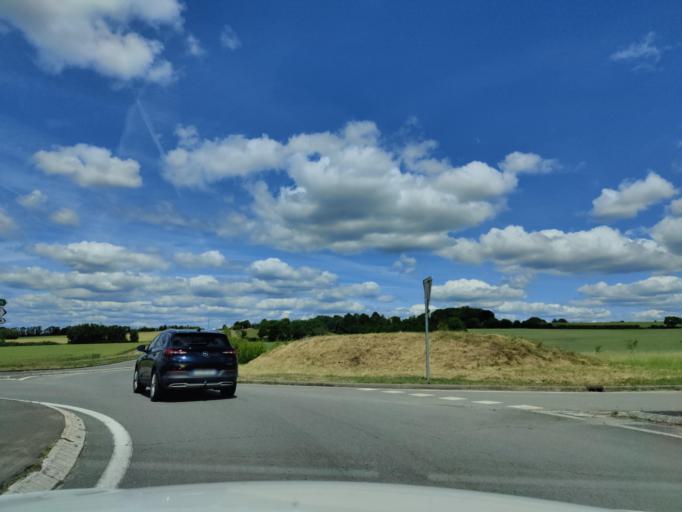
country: FR
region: Centre
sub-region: Departement du Cher
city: Fussy
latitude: 47.1775
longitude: 2.4240
